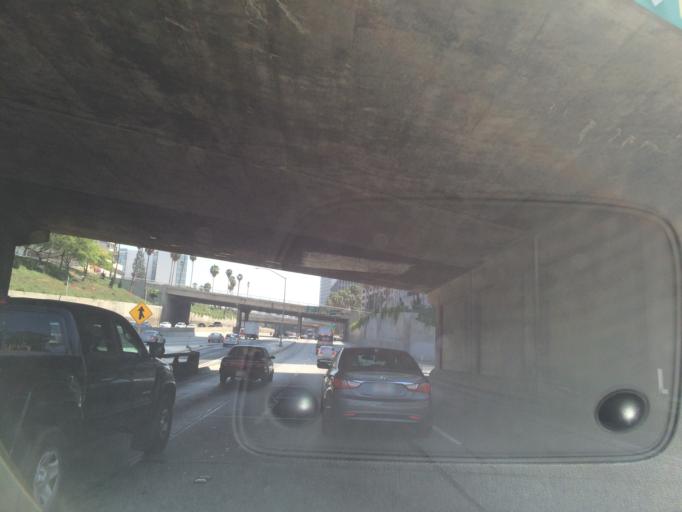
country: US
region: California
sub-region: Los Angeles County
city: Los Angeles
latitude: 34.0501
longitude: -118.2625
